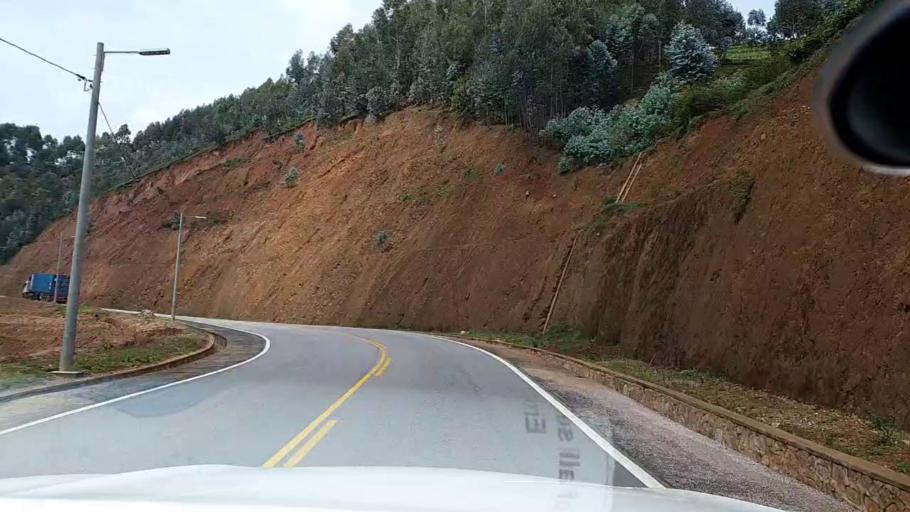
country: RW
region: Southern Province
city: Nzega
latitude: -2.5104
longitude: 29.4632
